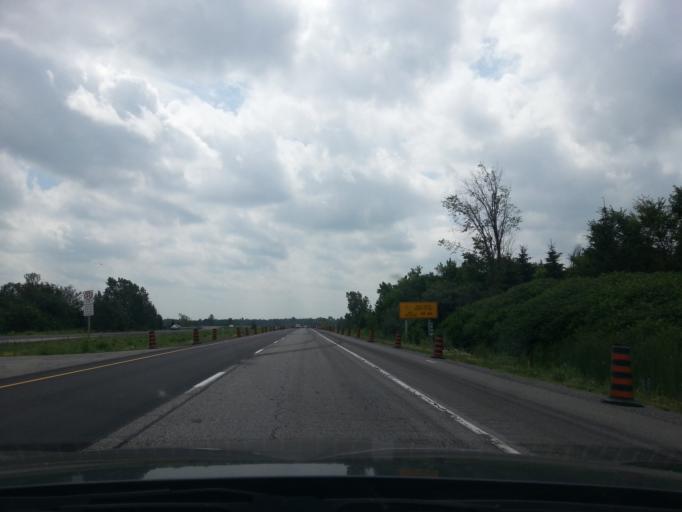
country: CA
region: Ontario
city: Bells Corners
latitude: 45.2571
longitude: -75.7864
